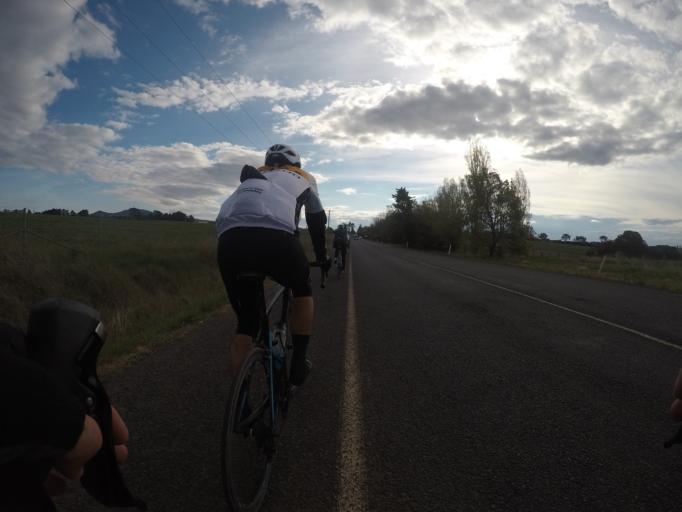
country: AU
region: New South Wales
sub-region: Orange Municipality
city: Orange
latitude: -33.2928
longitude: 149.0198
